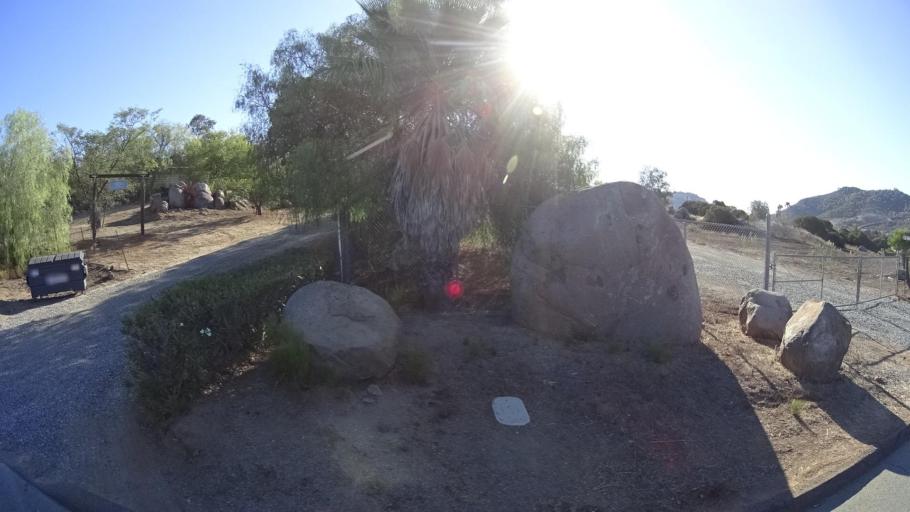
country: US
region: California
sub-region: San Diego County
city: Eucalyptus Hills
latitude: 32.9047
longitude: -116.9032
